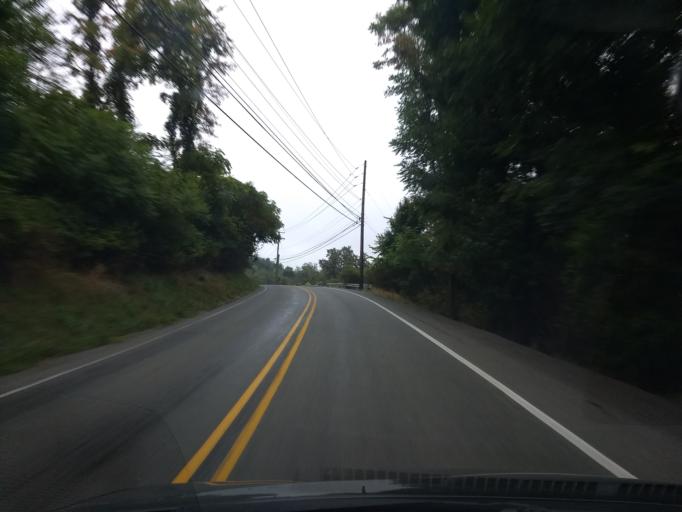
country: US
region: Pennsylvania
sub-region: Westmoreland County
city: Greensburg
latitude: 40.3086
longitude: -79.4897
